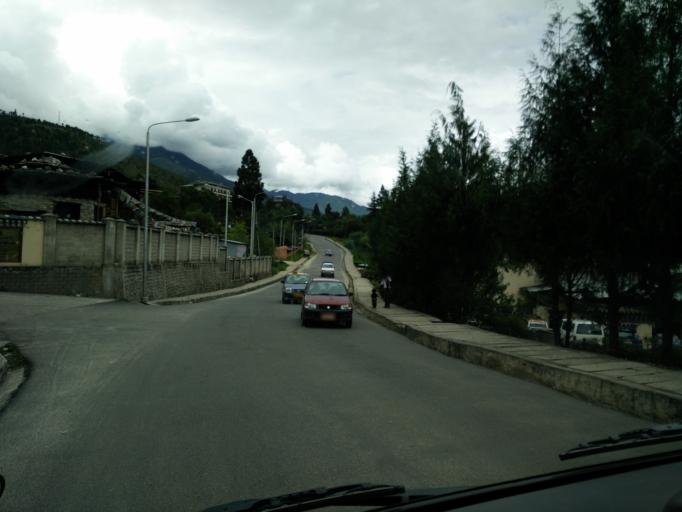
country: BT
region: Thimphu
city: Thimphu
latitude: 27.4711
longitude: 89.6314
